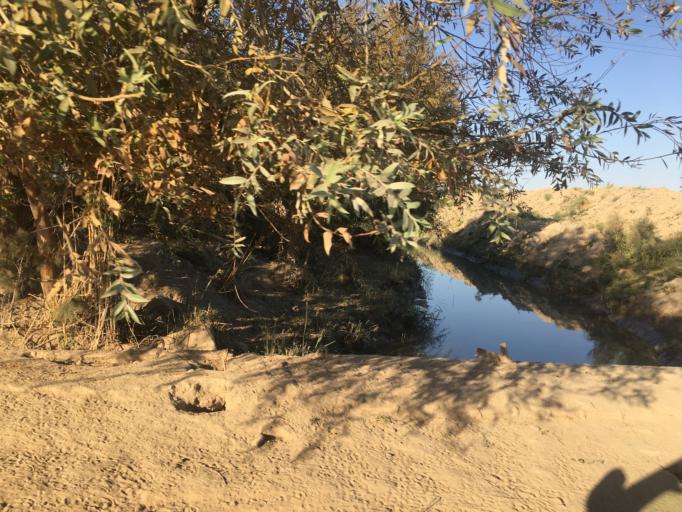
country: IR
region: Razavi Khorasan
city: Sarakhs
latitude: 37.0800
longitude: 61.2187
